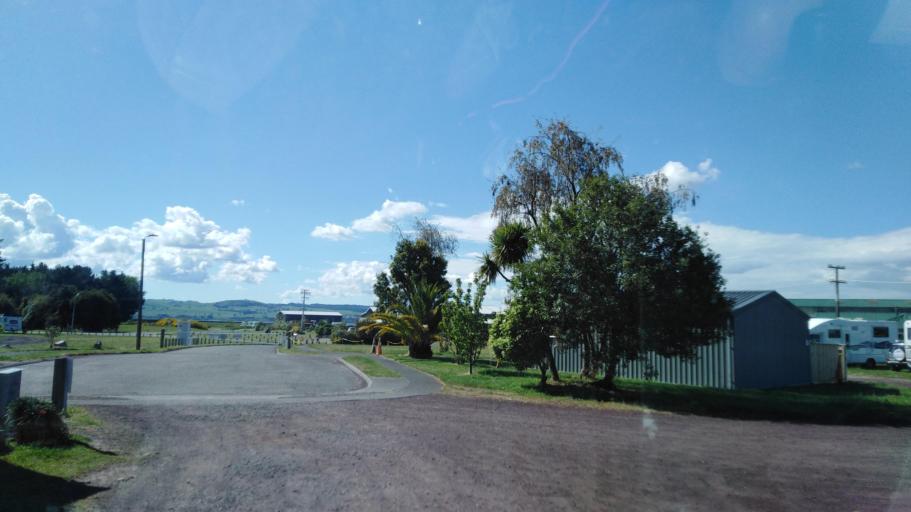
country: NZ
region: Waikato
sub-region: Taupo District
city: Taupo
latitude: -38.7397
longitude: 176.0807
